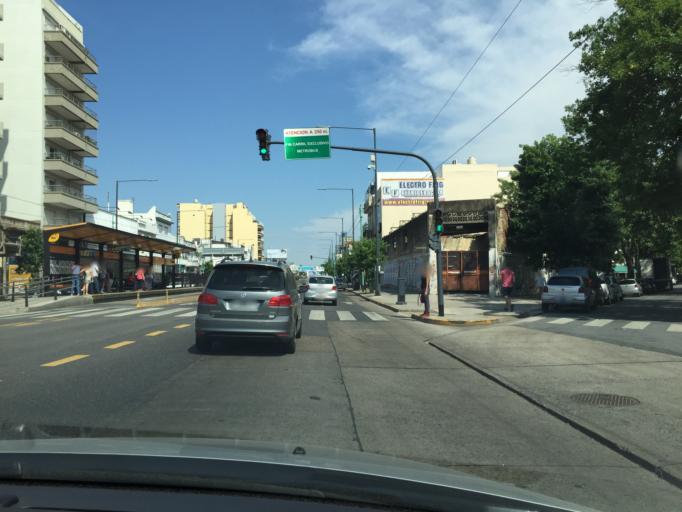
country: AR
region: Buenos Aires
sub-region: Partido de General San Martin
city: General San Martin
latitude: -34.5903
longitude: -58.5153
